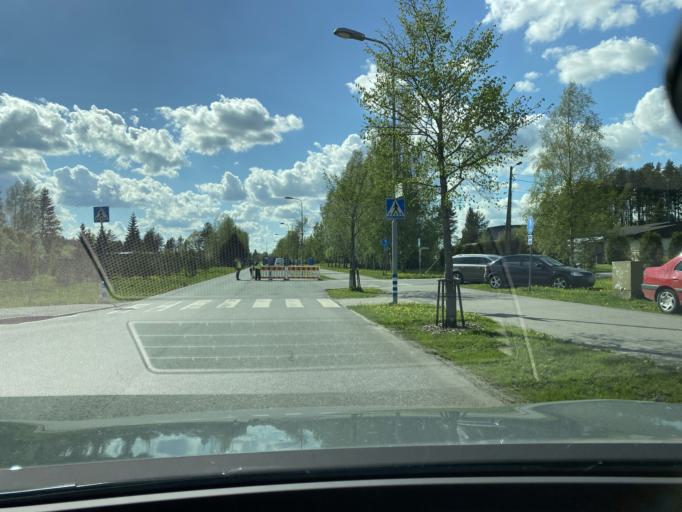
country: FI
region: Uusimaa
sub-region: Helsinki
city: Maentsaelae
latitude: 60.6457
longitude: 25.3239
